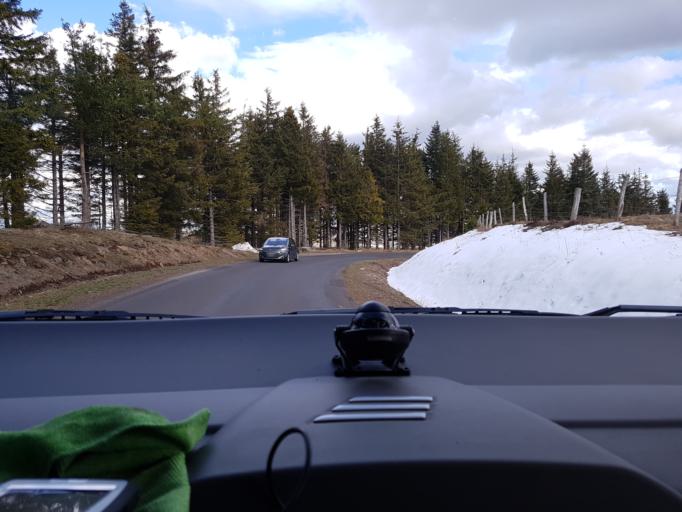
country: FR
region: Midi-Pyrenees
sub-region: Departement de l'Aveyron
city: Laguiole
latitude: 44.6599
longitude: 2.9459
